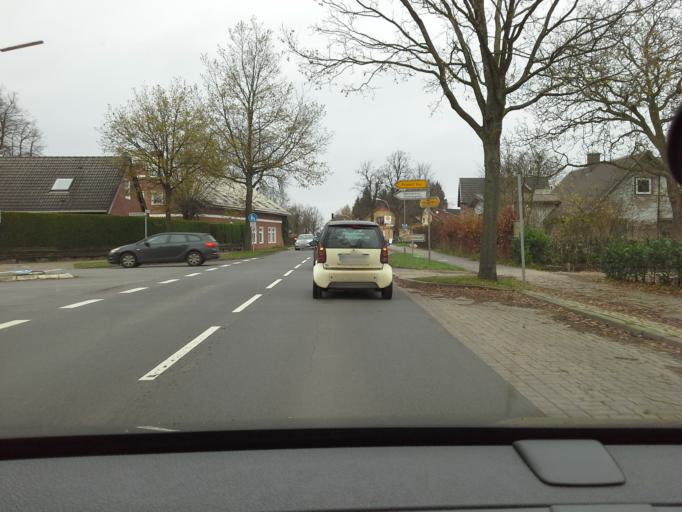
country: DE
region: Schleswig-Holstein
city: Kummerfeld
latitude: 53.6915
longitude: 9.7909
